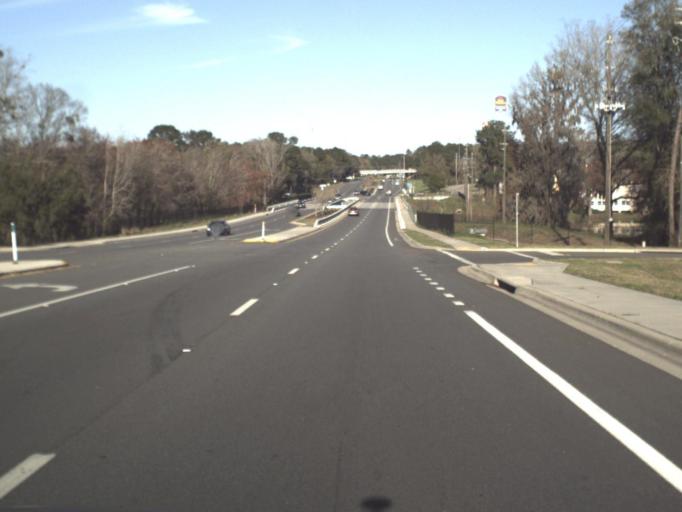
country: US
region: Florida
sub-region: Leon County
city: Tallahassee
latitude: 30.4822
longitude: -84.1666
